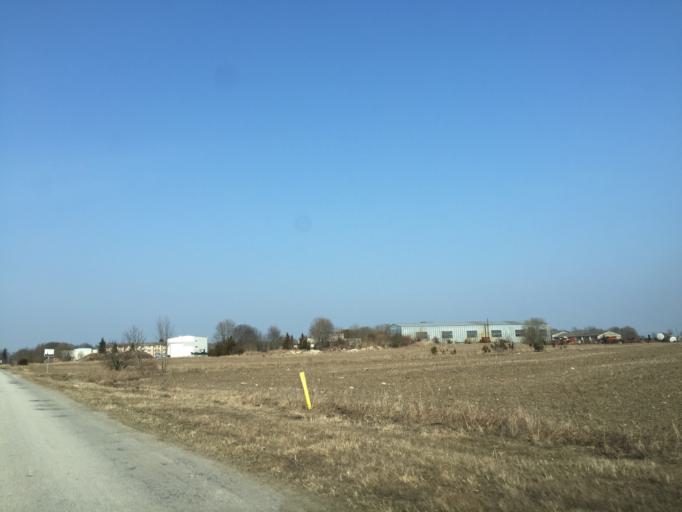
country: EE
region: Saare
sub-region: Orissaare vald
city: Orissaare
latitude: 58.4985
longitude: 23.1152
